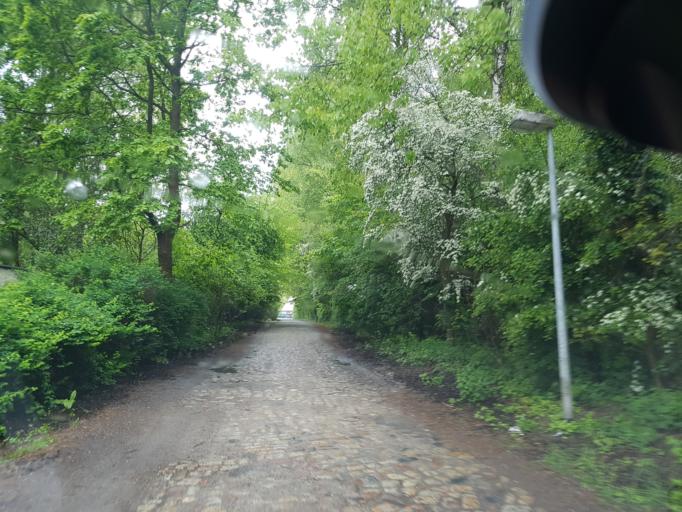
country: DE
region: Brandenburg
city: Tschernitz
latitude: 51.6176
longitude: 14.5905
